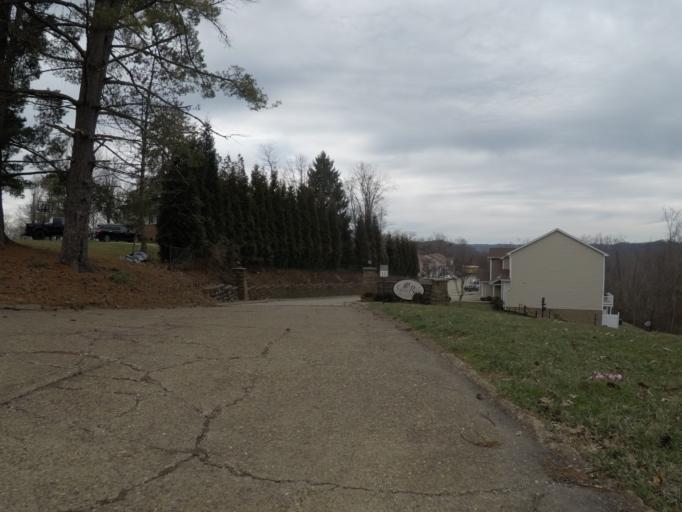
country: US
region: West Virginia
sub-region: Cabell County
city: Huntington
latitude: 38.3968
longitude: -82.3838
